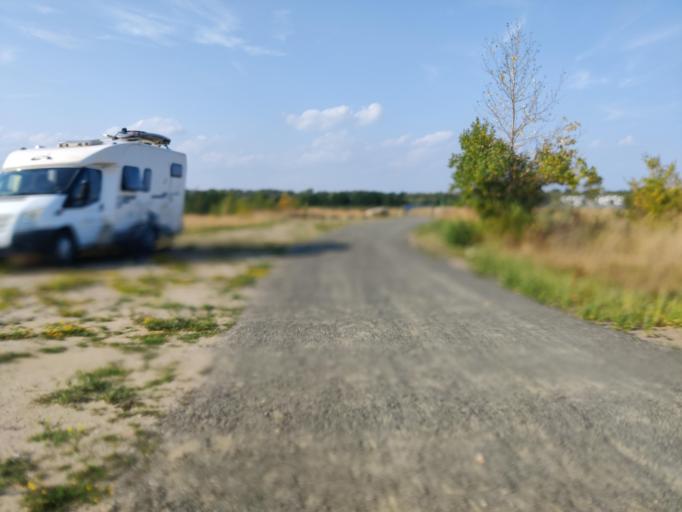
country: DE
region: Saxony
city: Neukieritzsch
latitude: 51.1711
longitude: 12.4339
